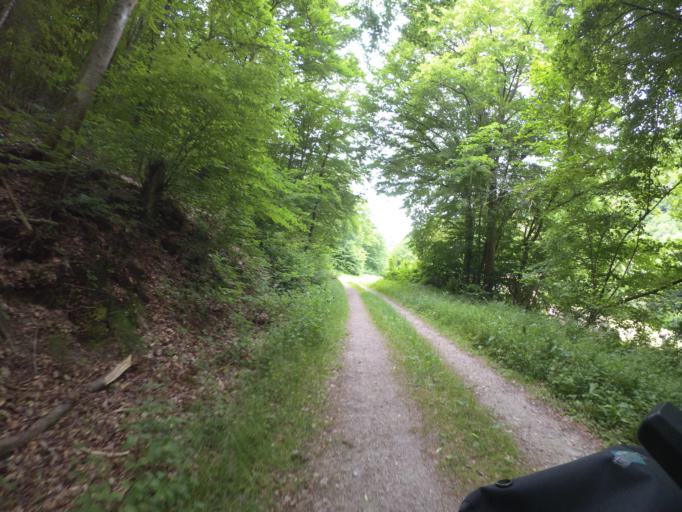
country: DE
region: Rheinland-Pfalz
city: Etgert
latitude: 49.7941
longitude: 7.0167
